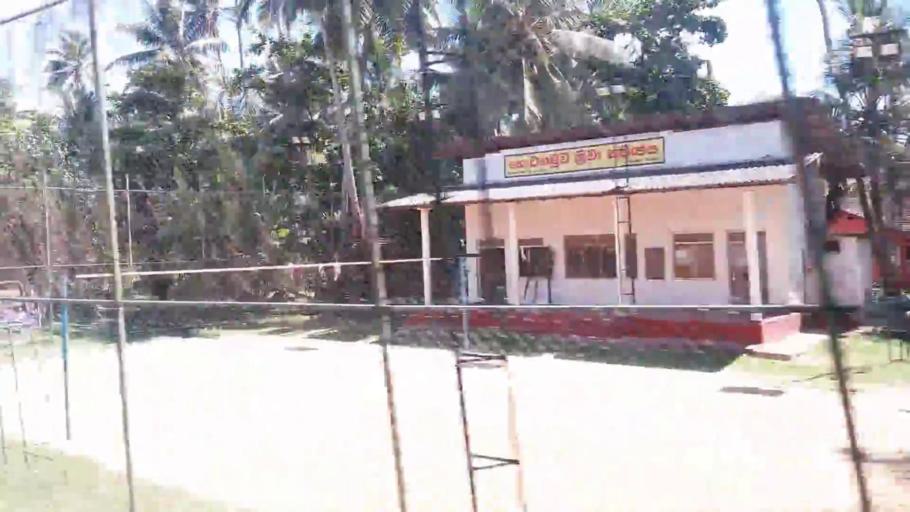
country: LK
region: Southern
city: Hikkaduwa
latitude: 6.1626
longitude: 80.0927
